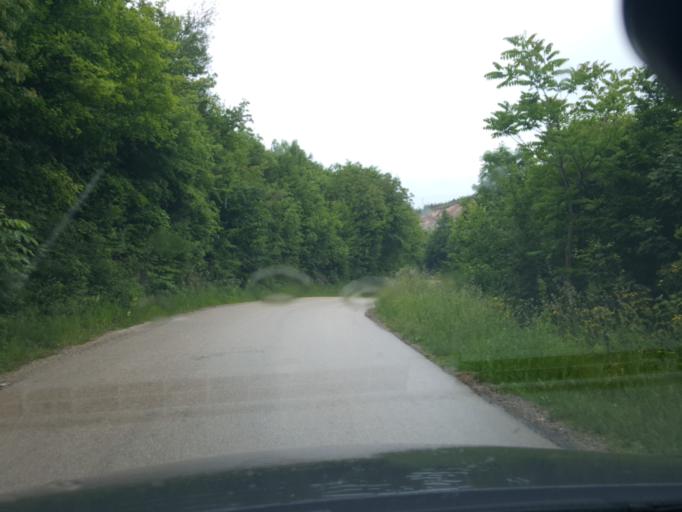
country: RS
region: Central Serbia
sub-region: Zajecarski Okrug
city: Boljevac
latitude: 43.7900
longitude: 21.9106
